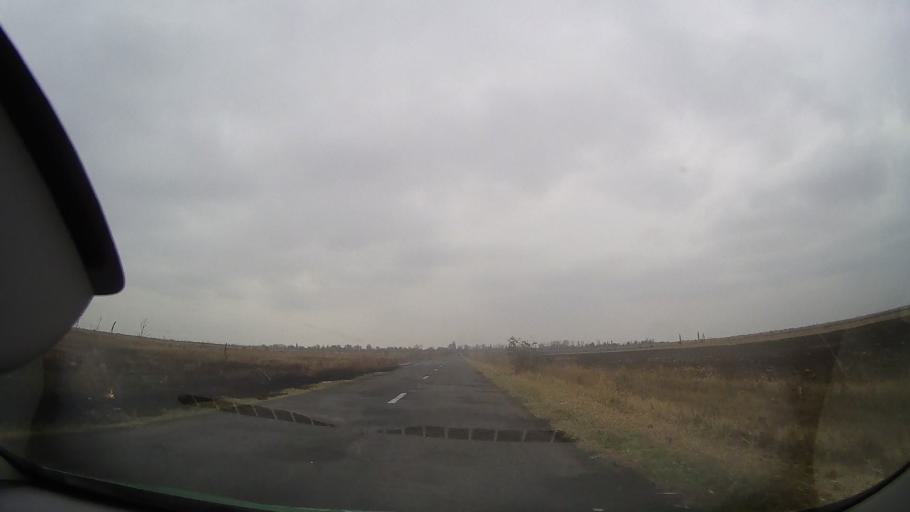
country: RO
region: Ialomita
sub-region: Comuna Garbovi
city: Garbovi
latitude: 44.7647
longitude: 26.7946
